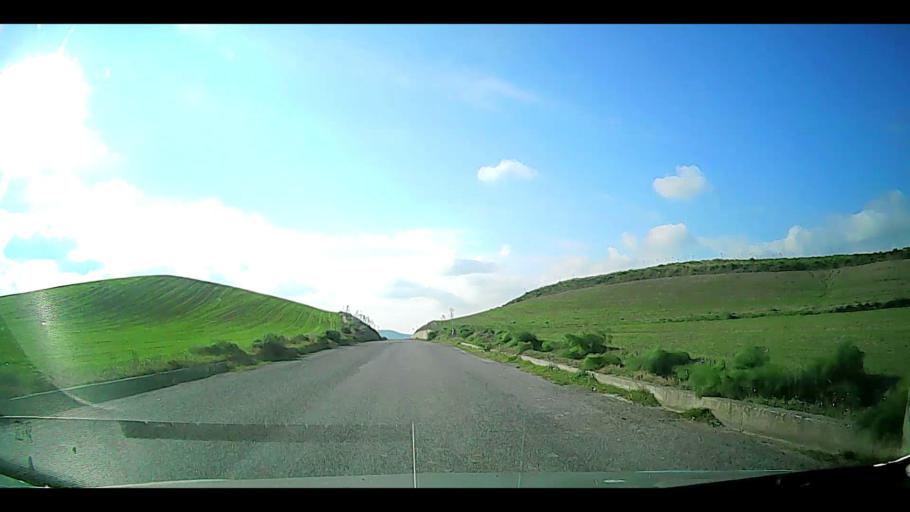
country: IT
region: Calabria
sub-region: Provincia di Crotone
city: Rocca di Neto
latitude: 39.1927
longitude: 17.0588
